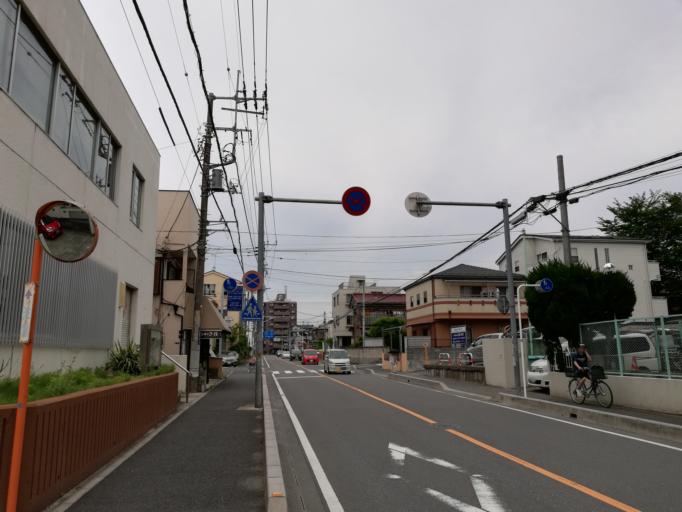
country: JP
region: Saitama
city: Shiki
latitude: 35.8274
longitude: 139.5786
